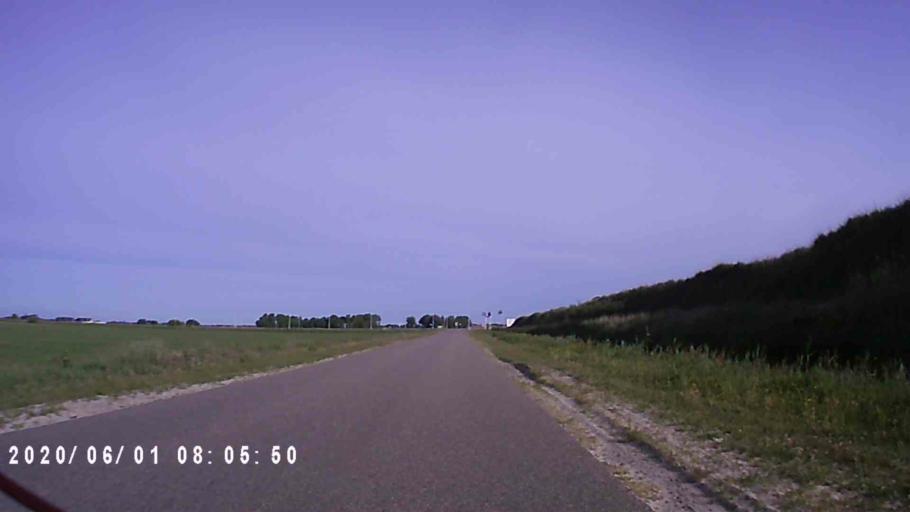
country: NL
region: Friesland
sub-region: Gemeente Tytsjerksteradiel
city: Oentsjerk
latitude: 53.2805
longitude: 5.9087
